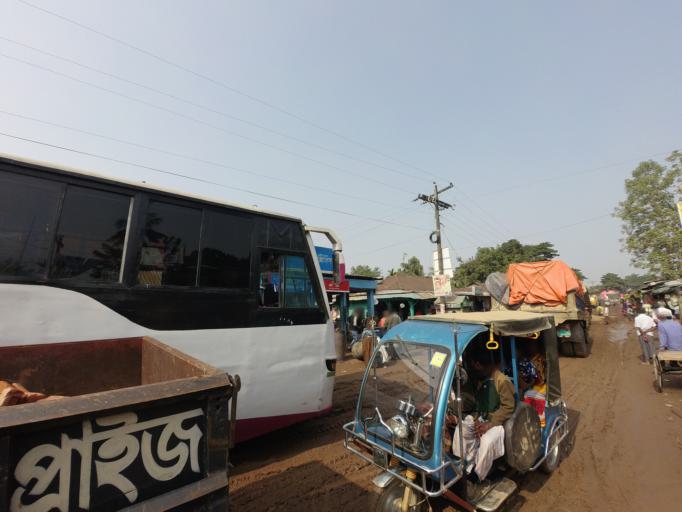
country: BD
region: Dhaka
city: Netrakona
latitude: 25.0137
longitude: 90.6472
